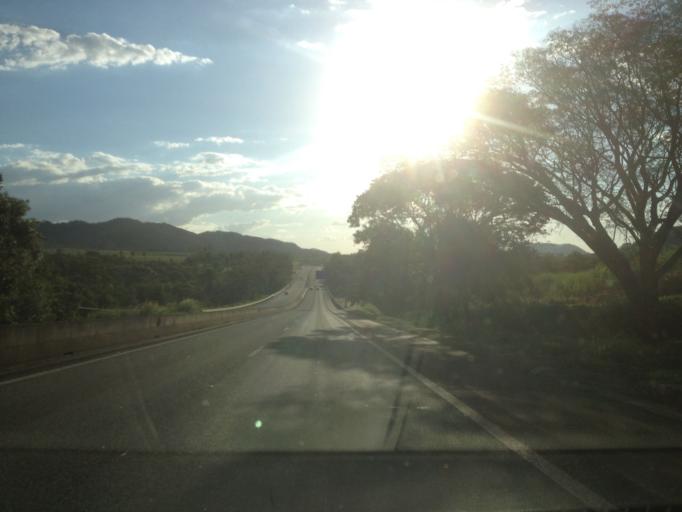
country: BR
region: Sao Paulo
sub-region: Brotas
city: Brotas
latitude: -22.2638
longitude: -48.2256
